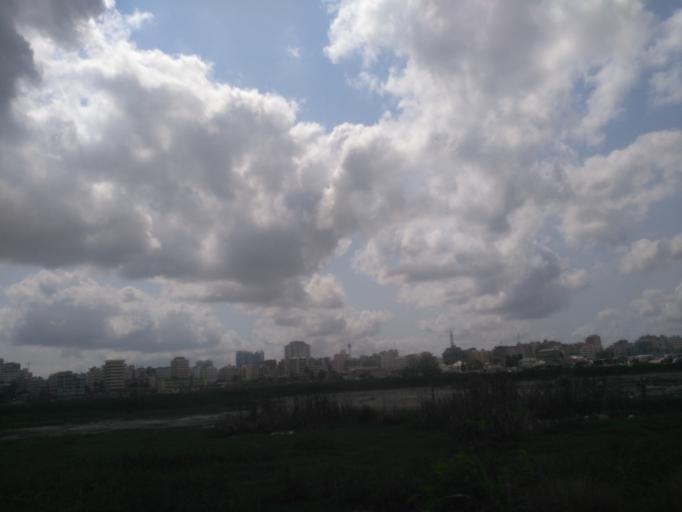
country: TZ
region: Dar es Salaam
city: Dar es Salaam
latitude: -6.8142
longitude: 39.2663
